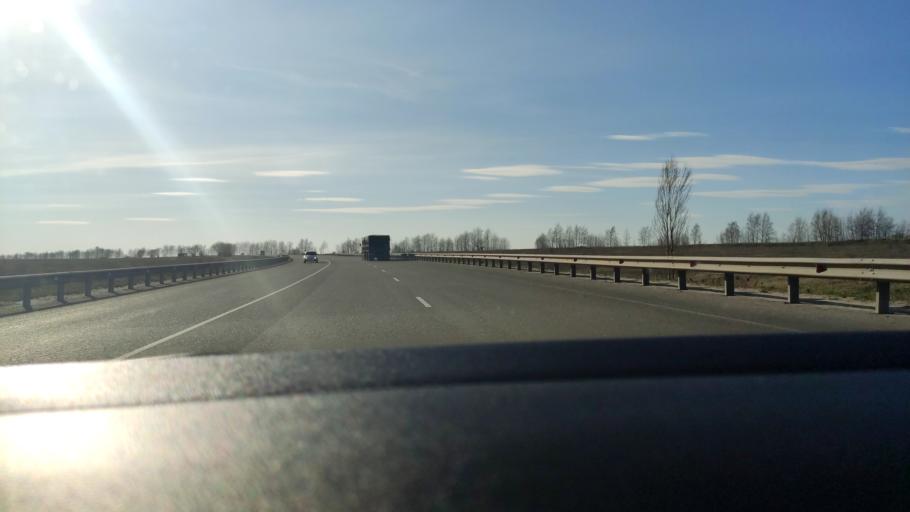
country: RU
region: Voronezj
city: Kolodeznyy
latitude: 51.3284
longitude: 39.1417
